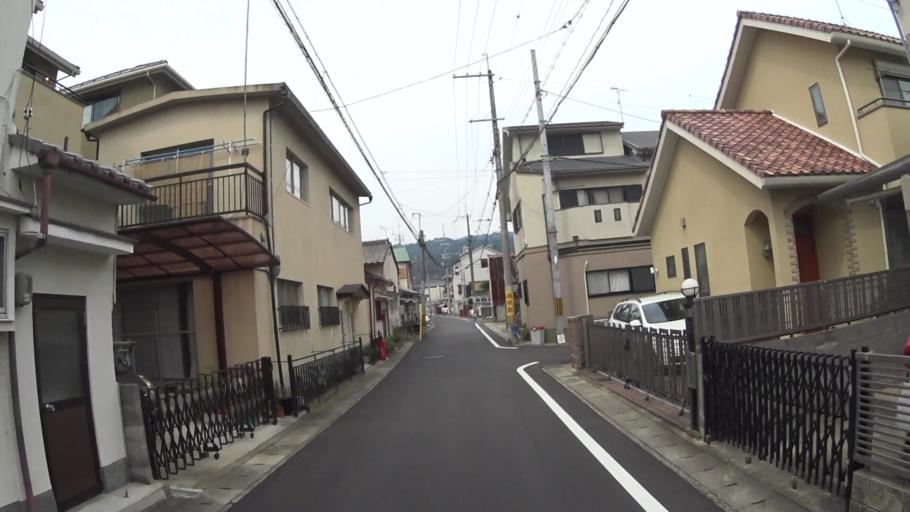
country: JP
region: Kyoto
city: Kyoto
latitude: 34.9913
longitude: 135.8000
